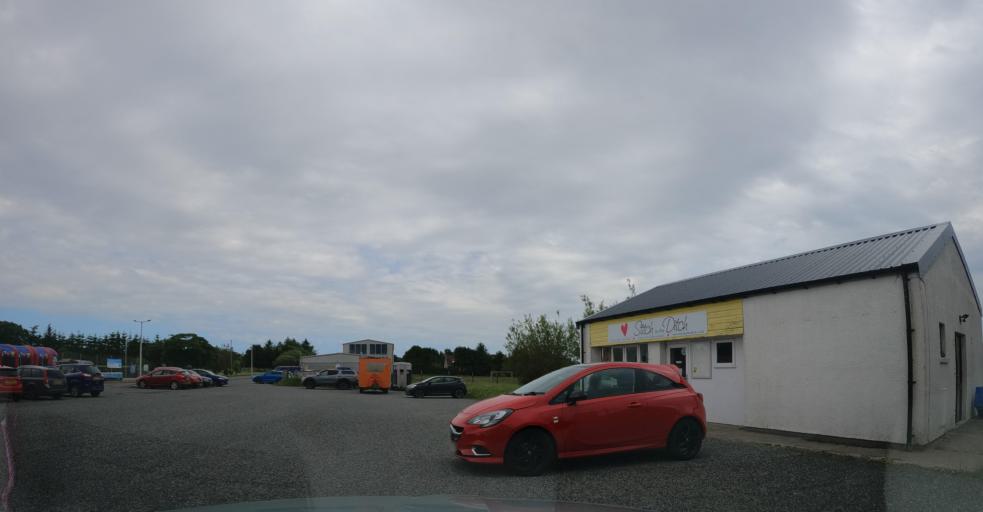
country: GB
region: Scotland
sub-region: Eilean Siar
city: Isle of Lewis
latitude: 58.2438
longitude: -6.3491
